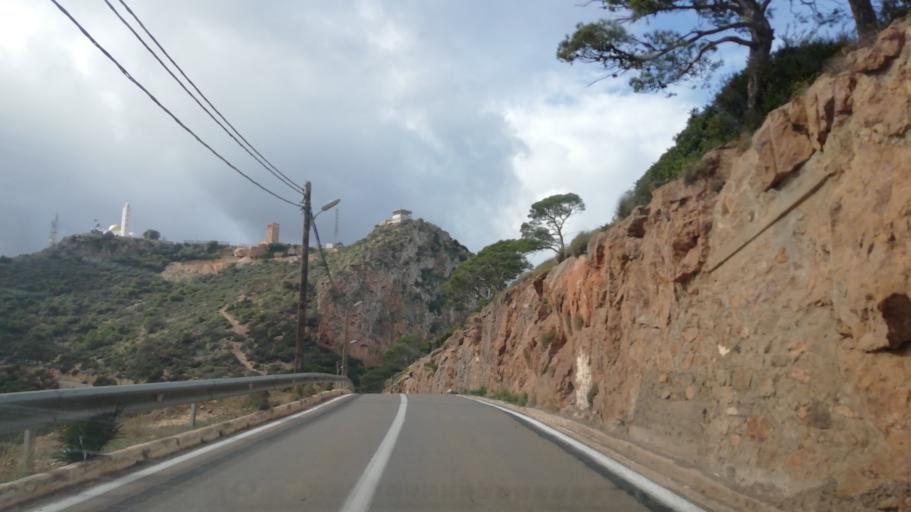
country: DZ
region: Oran
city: Oran
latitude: 35.7085
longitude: -0.6661
